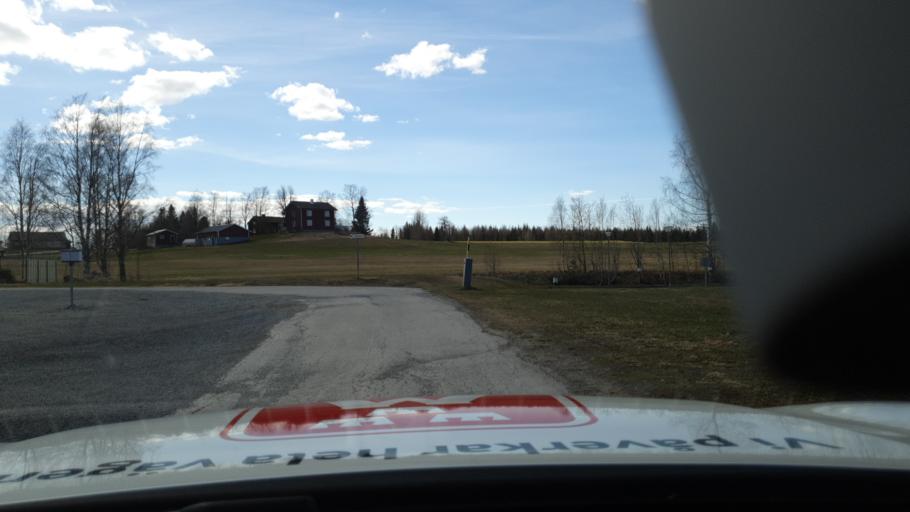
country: SE
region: Jaemtland
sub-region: Bergs Kommun
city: Hoverberg
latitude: 62.9997
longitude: 14.3335
